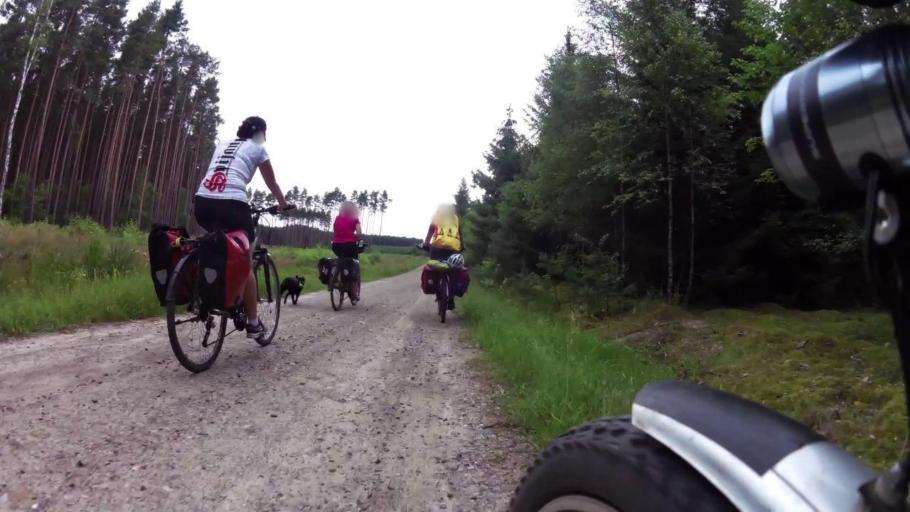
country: PL
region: West Pomeranian Voivodeship
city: Trzcinsko Zdroj
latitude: 52.8496
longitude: 14.6010
